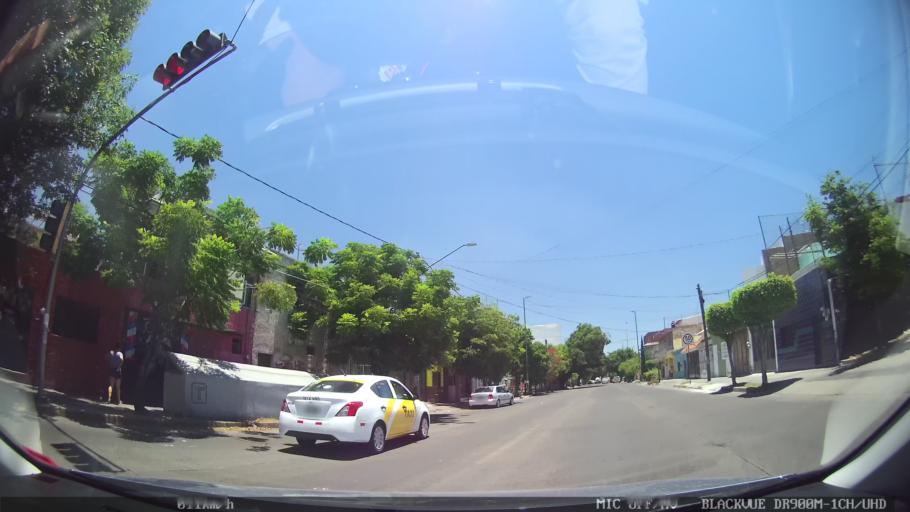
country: MX
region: Jalisco
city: Tlaquepaque
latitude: 20.6630
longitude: -103.2896
